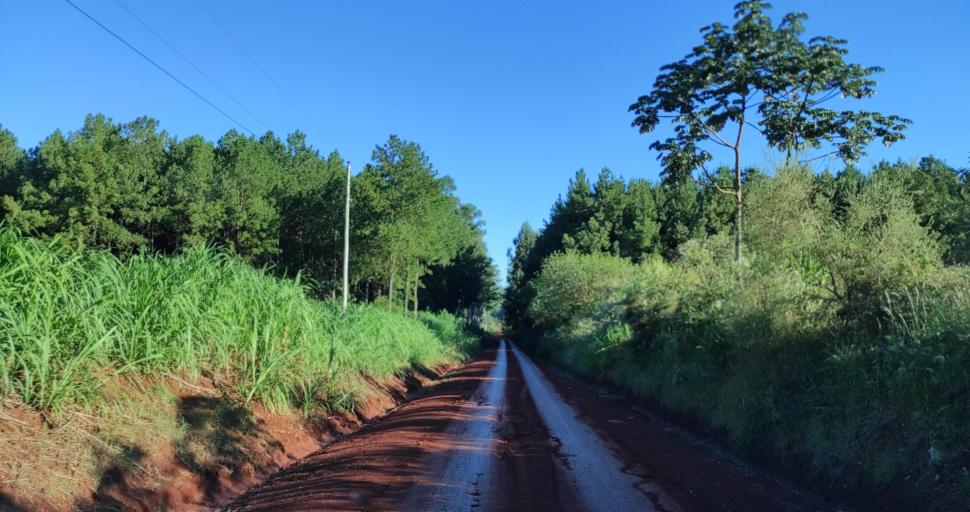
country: AR
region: Misiones
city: Puerto Rico
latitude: -26.8600
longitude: -55.0146
